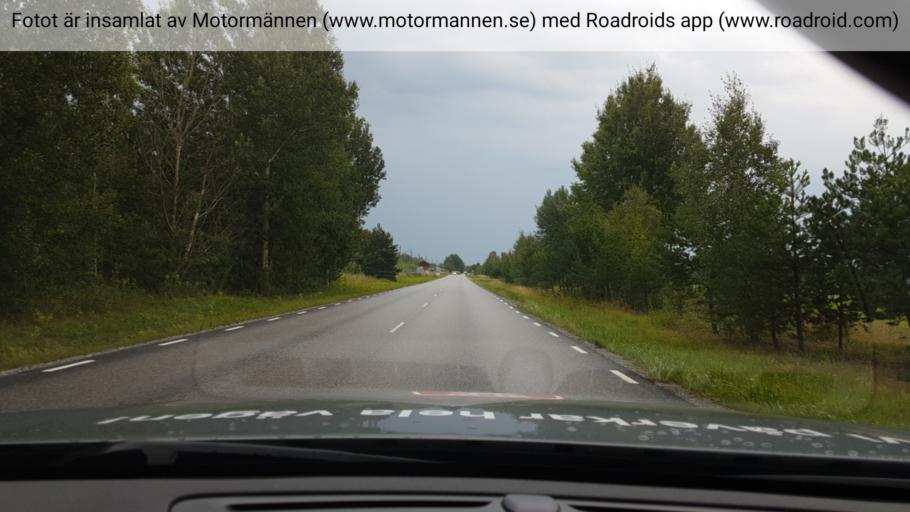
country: SE
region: Uppsala
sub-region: Habo Kommun
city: Balsta
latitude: 59.5359
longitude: 17.5712
